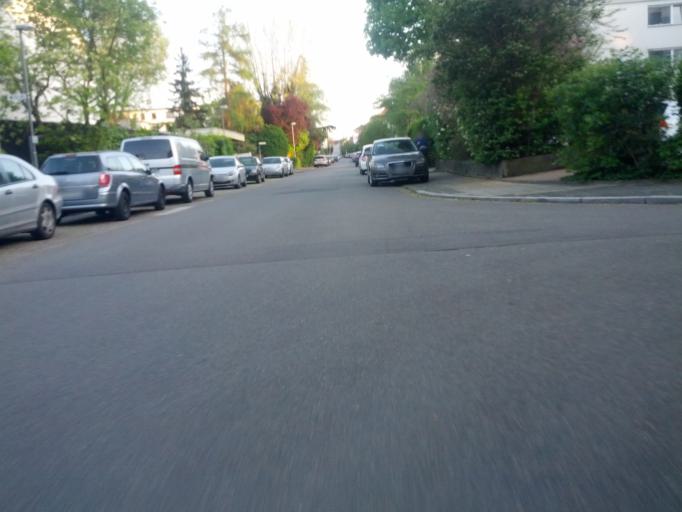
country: DE
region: Baden-Wuerttemberg
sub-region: Karlsruhe Region
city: Dossenheim
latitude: 49.4330
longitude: 8.6807
